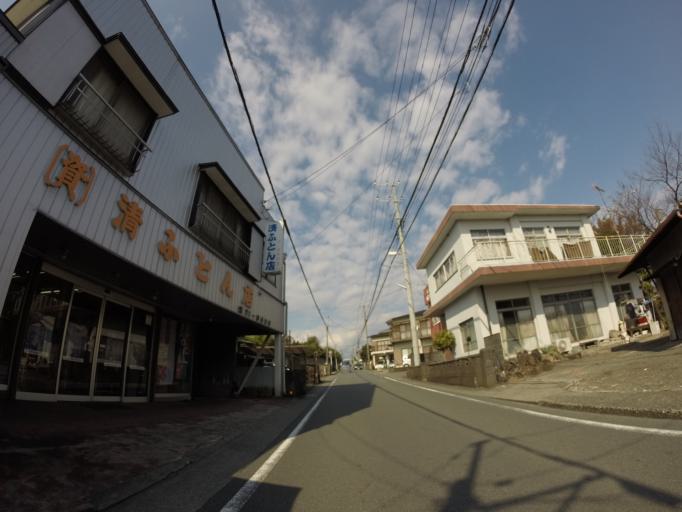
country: JP
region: Shizuoka
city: Fujinomiya
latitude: 35.1902
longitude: 138.6447
